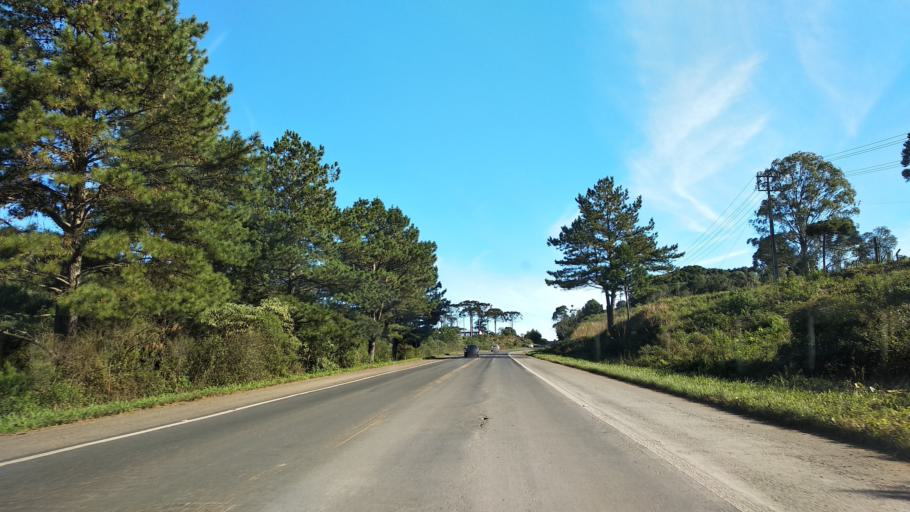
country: BR
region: Santa Catarina
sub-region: Campos Novos
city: Campos Novos
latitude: -27.4026
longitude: -51.2037
